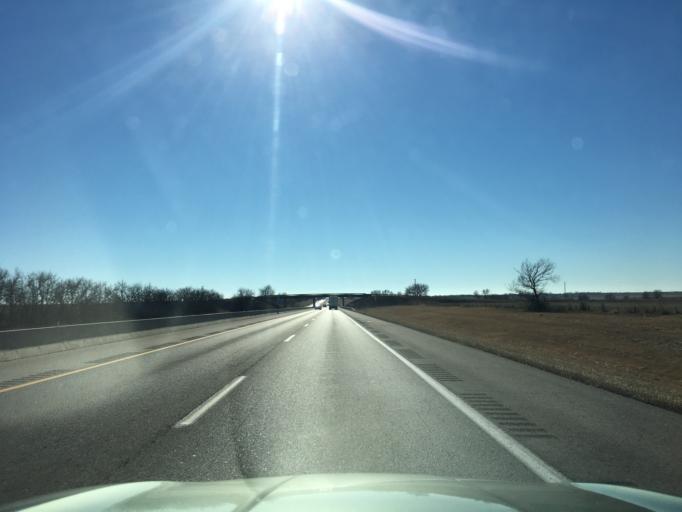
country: US
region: Kansas
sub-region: Sumner County
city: Wellington
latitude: 37.1184
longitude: -97.3389
